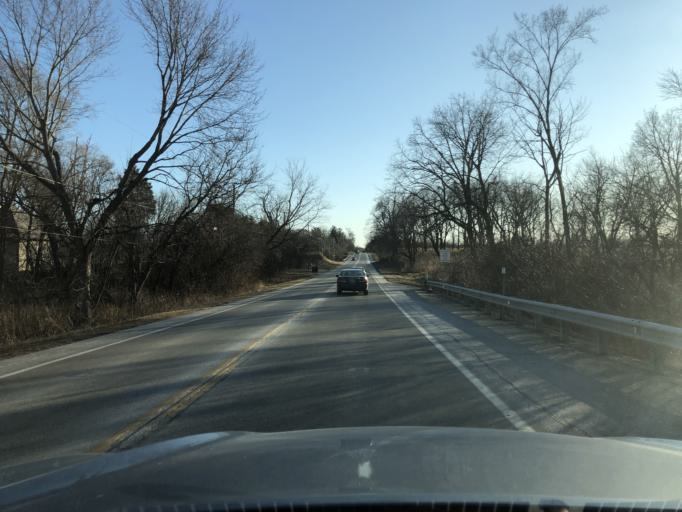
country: US
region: Illinois
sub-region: Lake County
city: Deer Park
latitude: 42.1694
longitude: -88.1017
